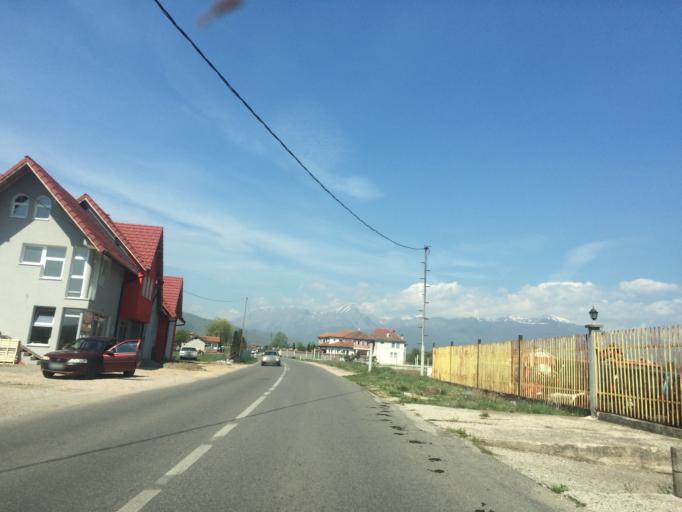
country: XK
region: Gjakova
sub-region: Komuna e Gjakoves
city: Gjakove
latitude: 42.3712
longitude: 20.3550
